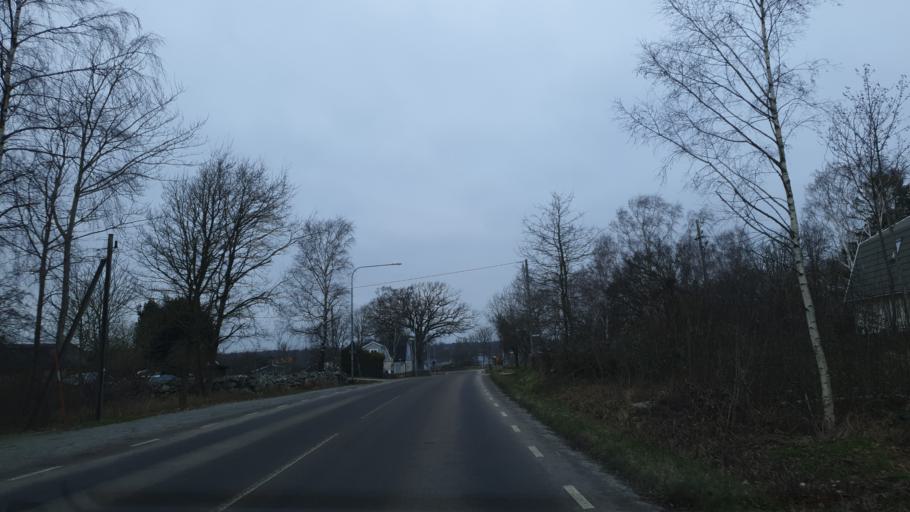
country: SE
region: Blekinge
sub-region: Karlskrona Kommun
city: Sturko
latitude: 56.1137
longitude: 15.6924
